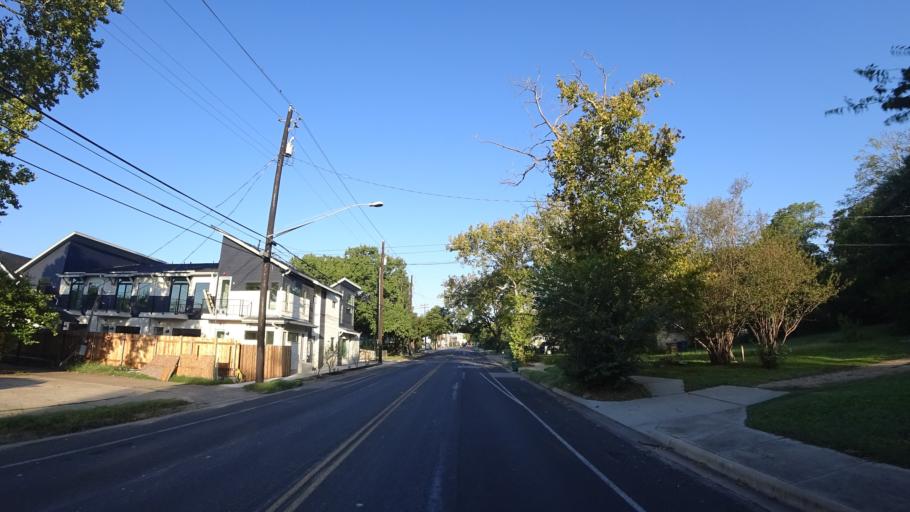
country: US
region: Texas
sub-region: Travis County
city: Austin
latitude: 30.3381
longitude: -97.7150
